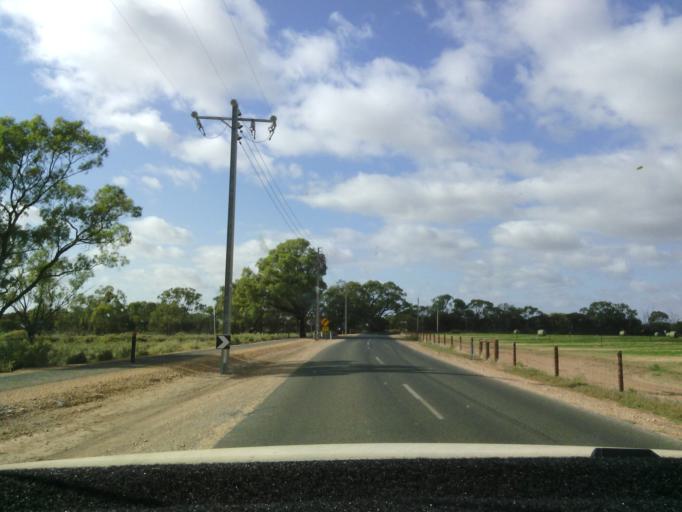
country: AU
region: South Australia
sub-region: Berri and Barmera
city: Berri
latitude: -34.2802
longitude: 140.6258
